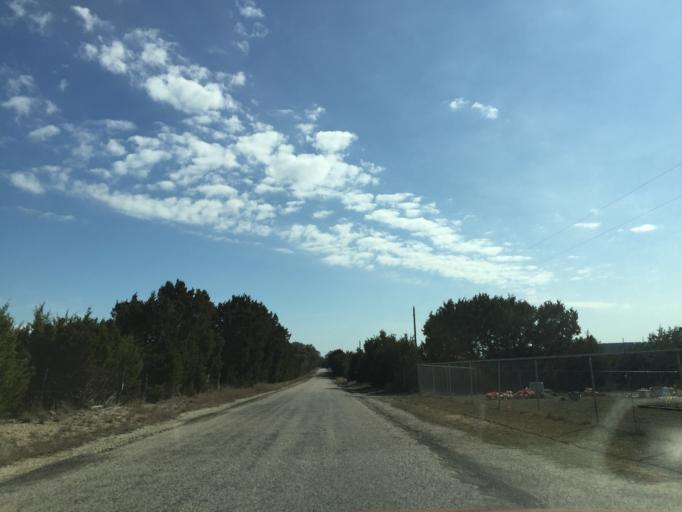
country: US
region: Texas
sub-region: Williamson County
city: Florence
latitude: 30.7791
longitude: -97.8908
